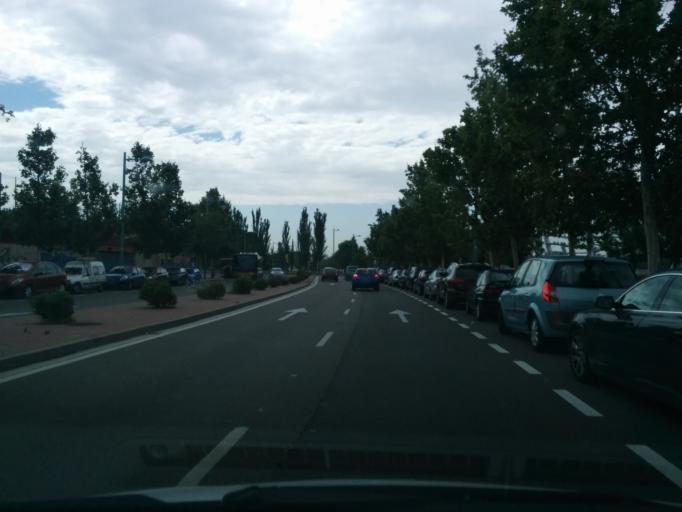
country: ES
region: Aragon
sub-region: Provincia de Zaragoza
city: Almozara
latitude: 41.6675
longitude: -0.8958
